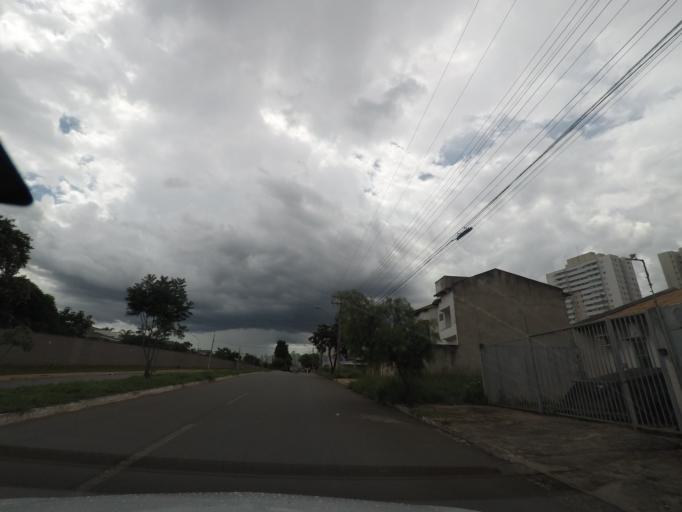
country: BR
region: Goias
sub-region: Goiania
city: Goiania
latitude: -16.7152
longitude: -49.3227
